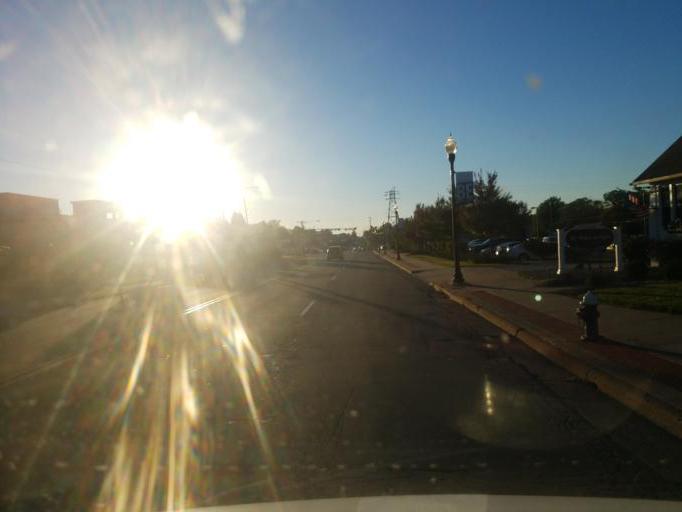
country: US
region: Ohio
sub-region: Stark County
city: Alliance
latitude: 40.9018
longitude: -81.1137
